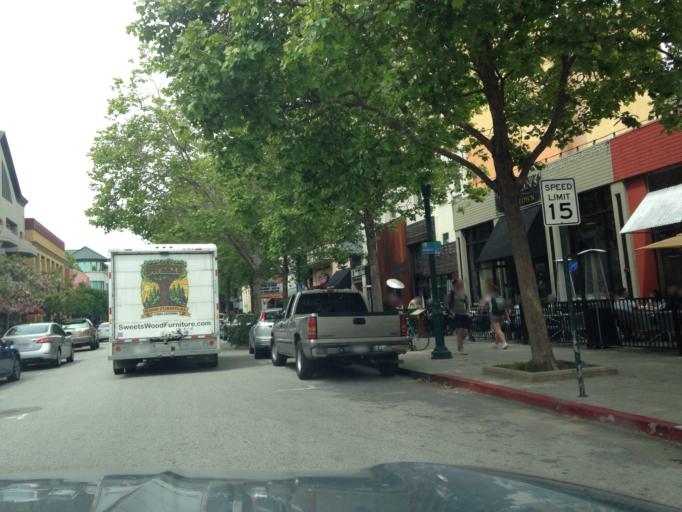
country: US
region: California
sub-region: Santa Cruz County
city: Santa Cruz
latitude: 36.9718
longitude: -122.0255
